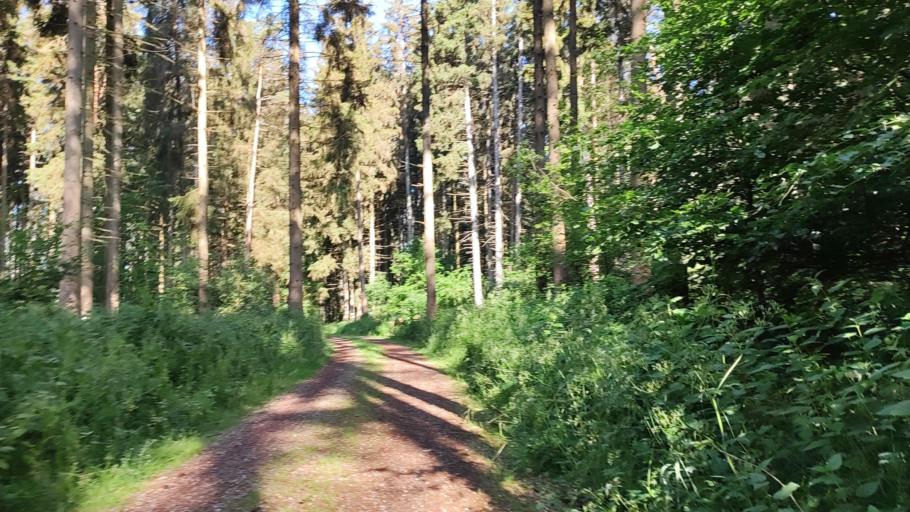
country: DE
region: Bavaria
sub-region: Swabia
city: Horgau
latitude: 48.3811
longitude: 10.7036
